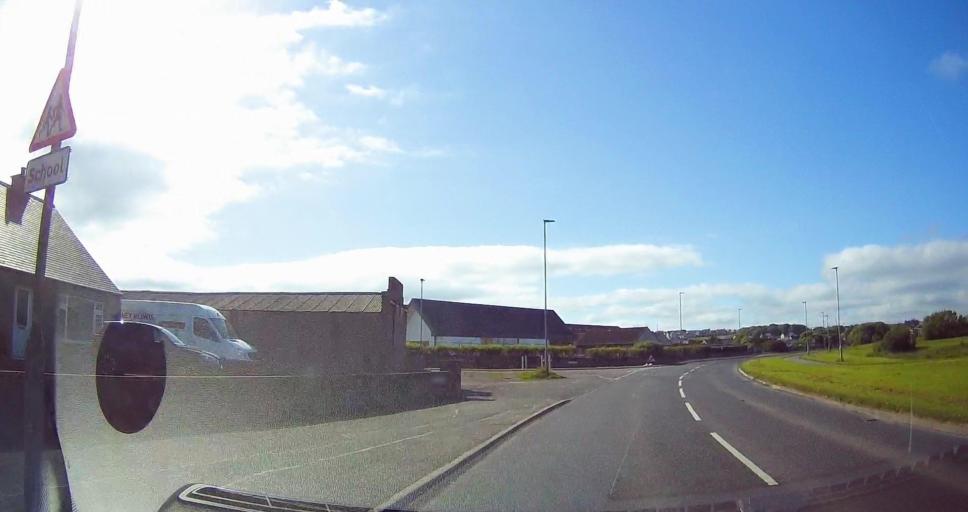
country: GB
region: Scotland
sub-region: Orkney Islands
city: Orkney
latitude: 58.9814
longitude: -2.9680
